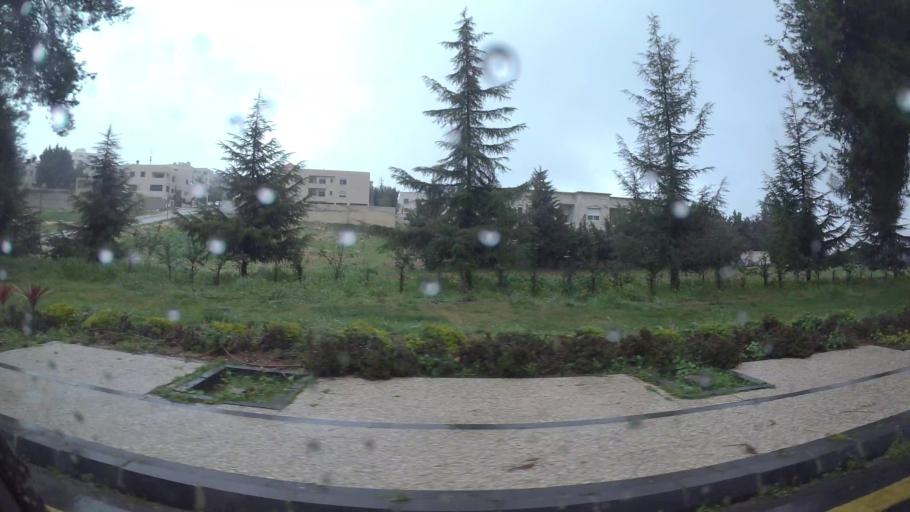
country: JO
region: Amman
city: Wadi as Sir
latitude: 31.9968
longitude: 35.8171
